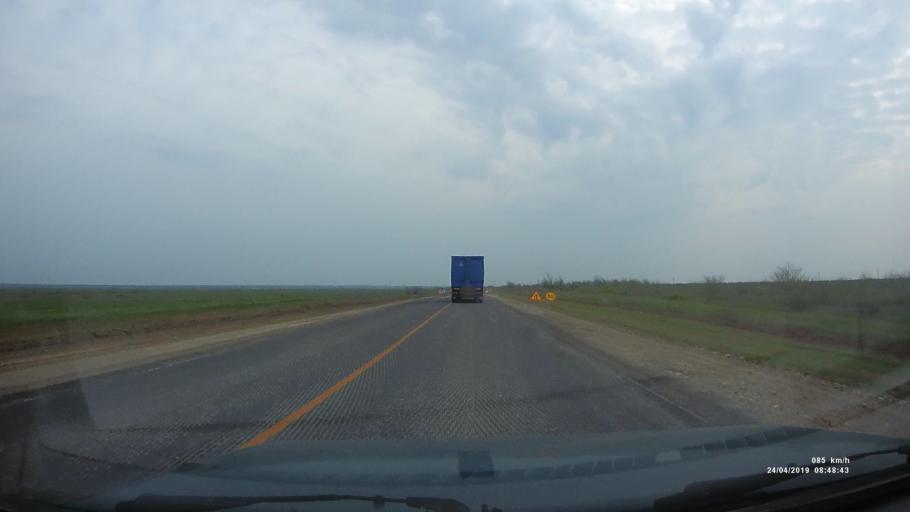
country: RU
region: Kalmykiya
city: Arshan'
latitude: 46.2528
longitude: 44.1131
